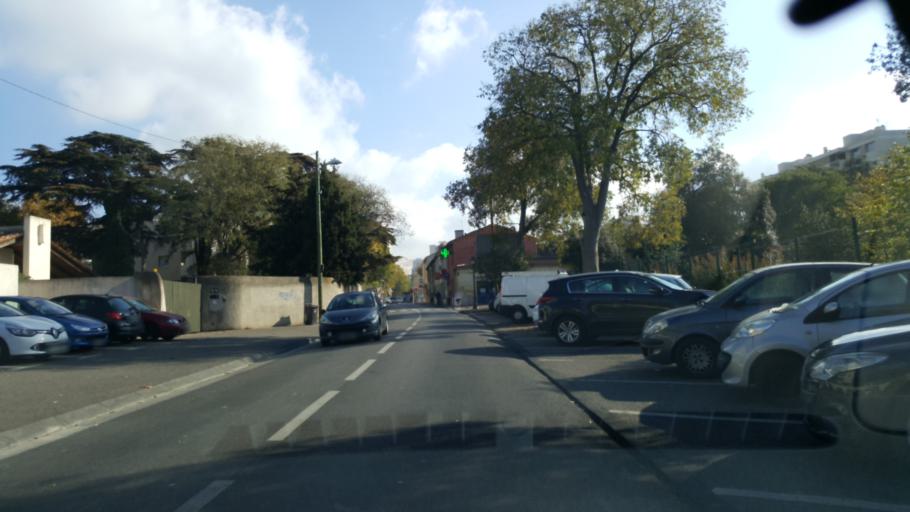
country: FR
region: Provence-Alpes-Cote d'Azur
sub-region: Departement des Bouches-du-Rhone
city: Marseille 09
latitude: 43.2599
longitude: 5.4161
